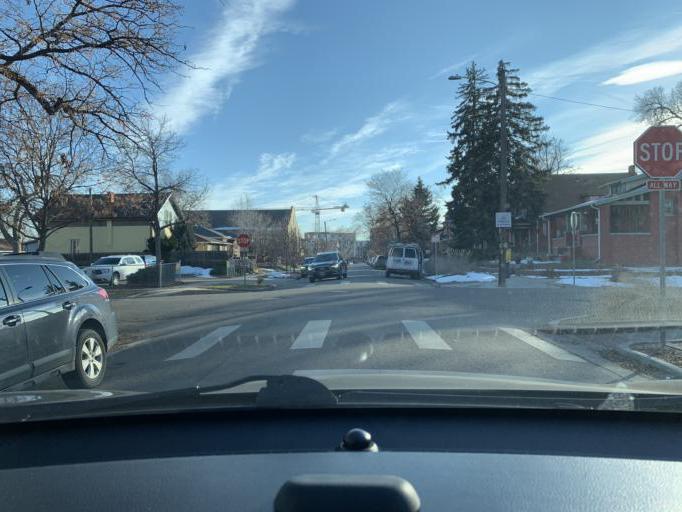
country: US
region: Colorado
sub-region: Adams County
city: Berkley
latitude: 39.7721
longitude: -105.0330
